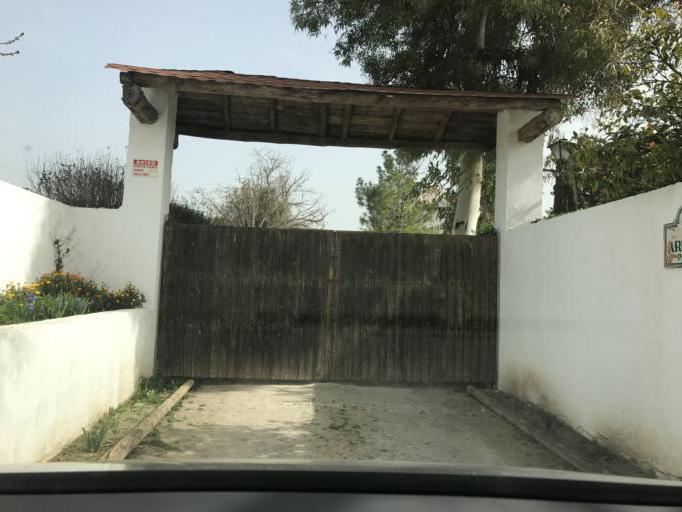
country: ES
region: Andalusia
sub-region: Provincia de Granada
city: Atarfe
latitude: 37.1979
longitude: -3.6708
